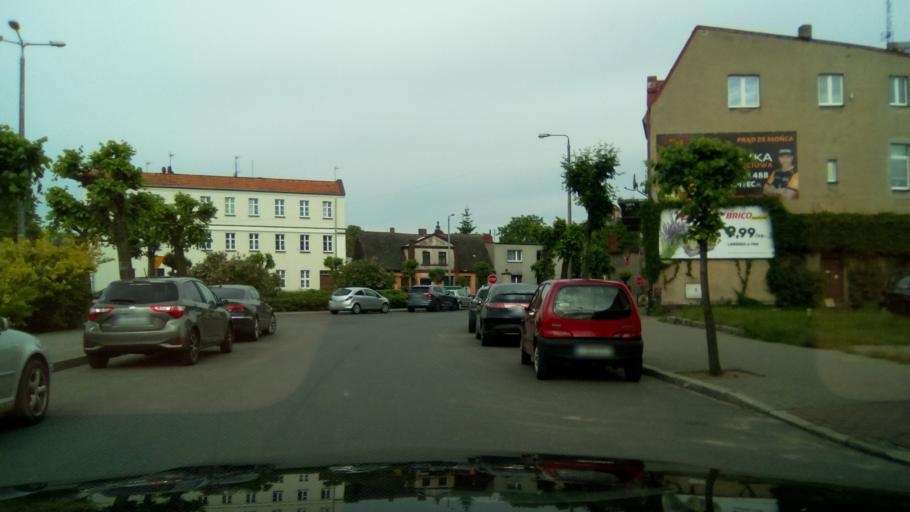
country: PL
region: Kujawsko-Pomorskie
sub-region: Powiat zninski
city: Janowiec Wielkopolski
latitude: 52.7569
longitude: 17.4888
